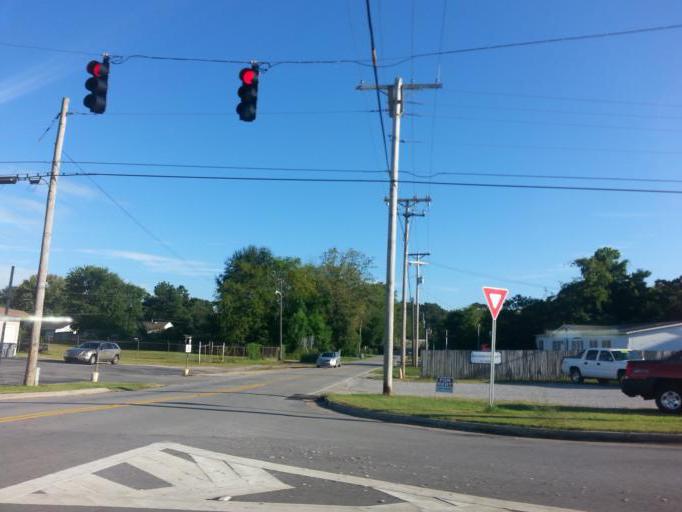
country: US
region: Alabama
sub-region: Lauderdale County
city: East Florence
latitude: 34.8312
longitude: -87.6212
